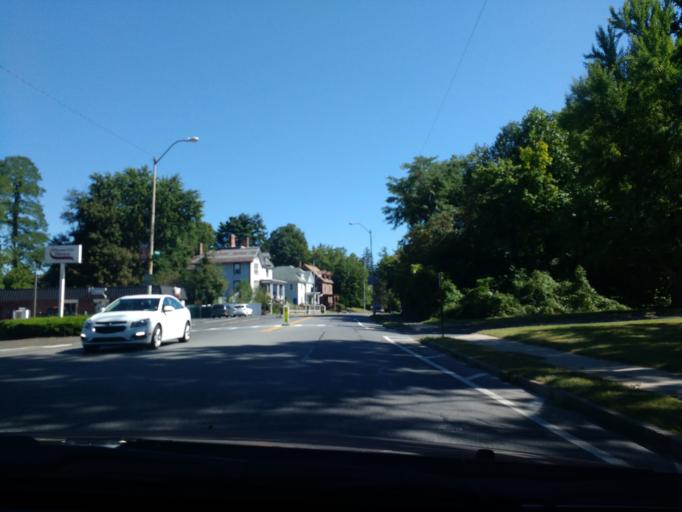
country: US
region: New York
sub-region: Ulster County
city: Kingston
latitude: 41.9253
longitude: -73.9905
